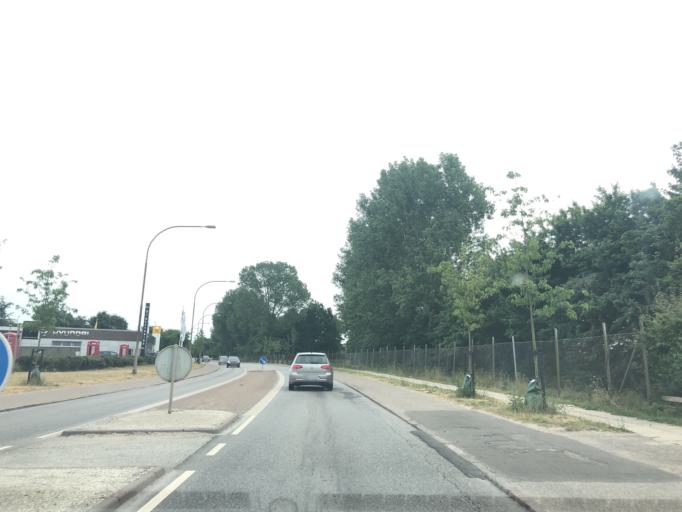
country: DK
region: Zealand
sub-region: Koge Kommune
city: Koge
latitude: 55.4703
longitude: 12.1724
